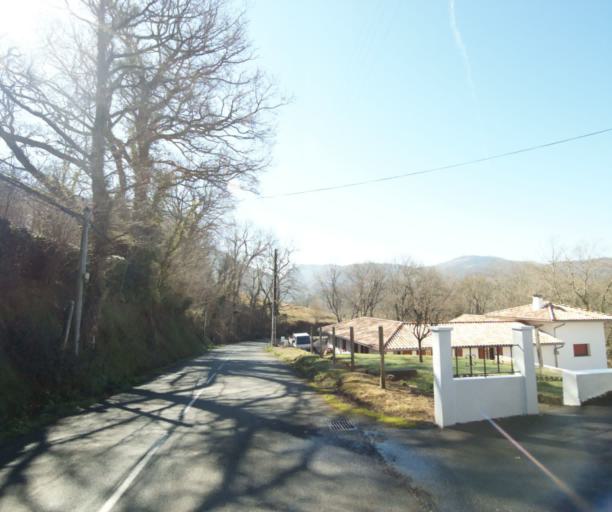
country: FR
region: Aquitaine
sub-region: Departement des Pyrenees-Atlantiques
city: Urrugne
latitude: 43.3449
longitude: -1.6665
